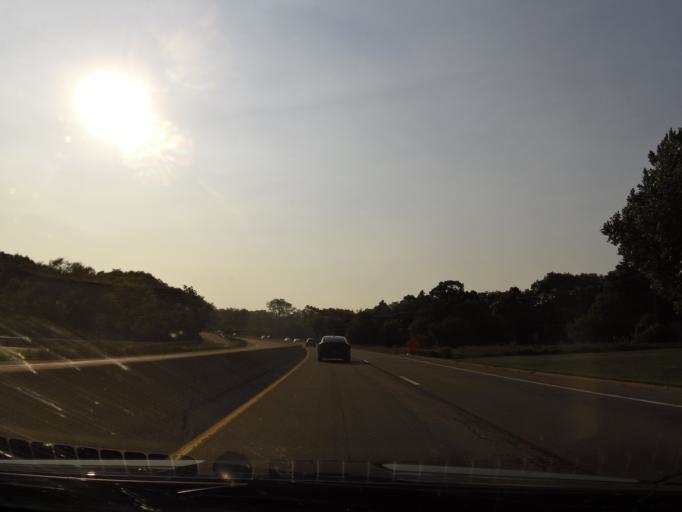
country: US
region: Minnesota
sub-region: Hennepin County
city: Minnetonka
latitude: 44.9118
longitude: -93.5184
